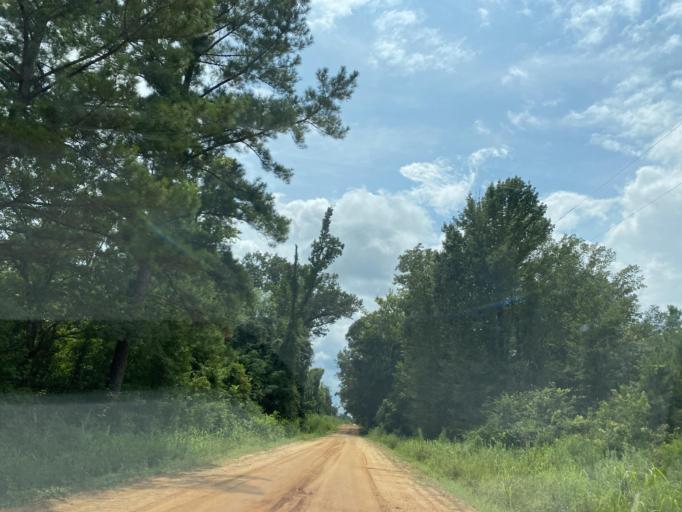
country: US
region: Georgia
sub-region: Wilcox County
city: Abbeville
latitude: 32.0943
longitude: -83.2729
